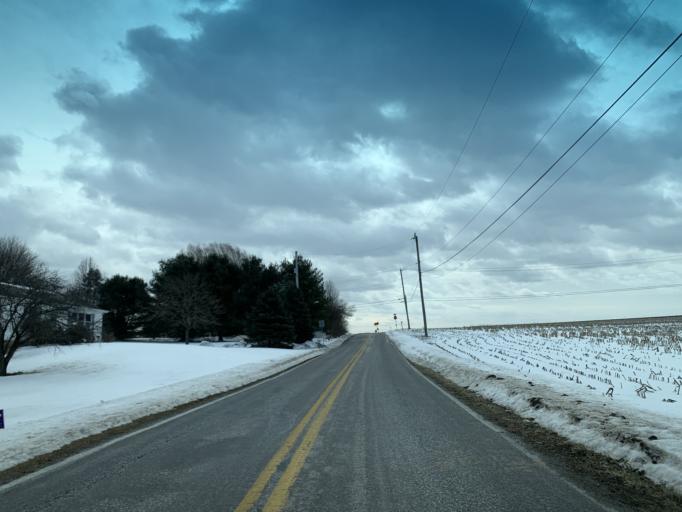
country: US
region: Pennsylvania
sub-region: York County
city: Shrewsbury
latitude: 39.7855
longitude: -76.6450
